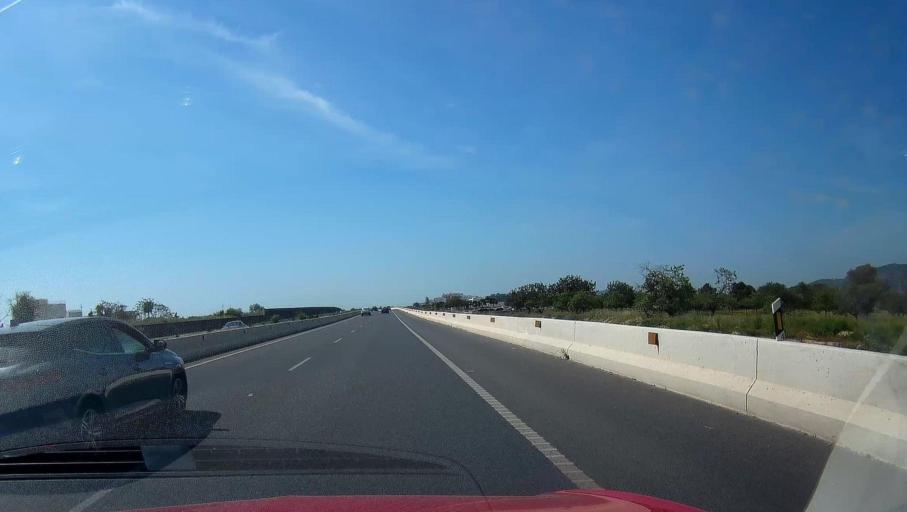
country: ES
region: Balearic Islands
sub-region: Illes Balears
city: Ibiza
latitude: 38.9478
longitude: 1.4433
